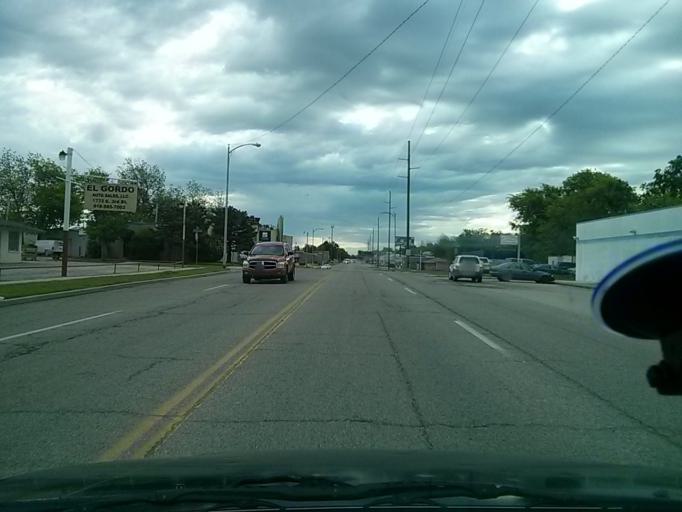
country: US
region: Oklahoma
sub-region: Tulsa County
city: Tulsa
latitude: 36.1567
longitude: -95.9666
